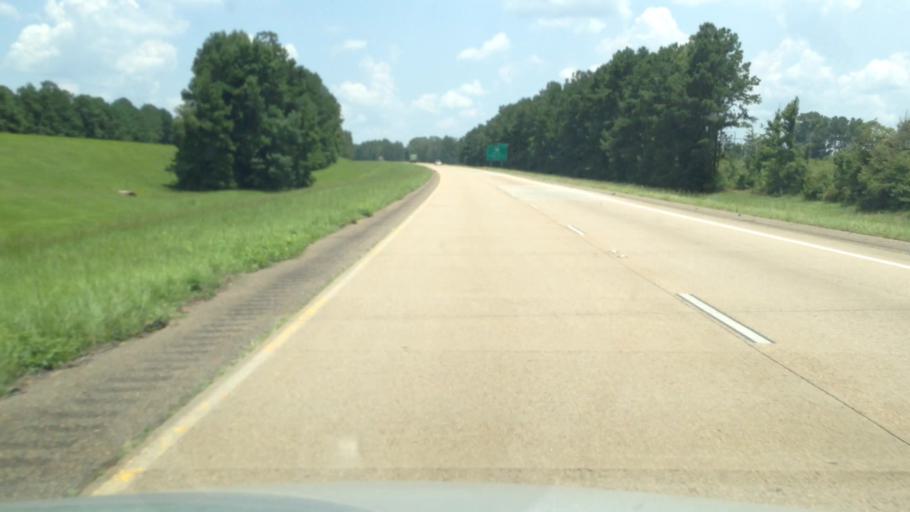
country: US
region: Louisiana
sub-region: Rapides Parish
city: Lecompte
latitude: 31.0329
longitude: -92.4109
